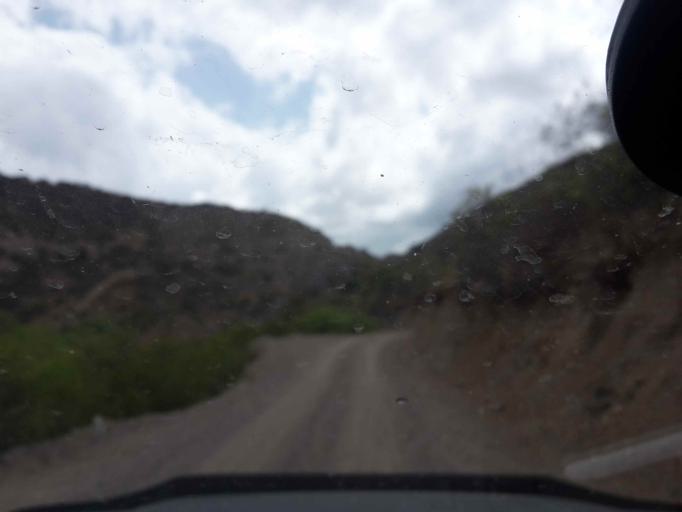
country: BO
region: Cochabamba
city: Sipe Sipe
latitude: -17.5220
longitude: -66.5540
